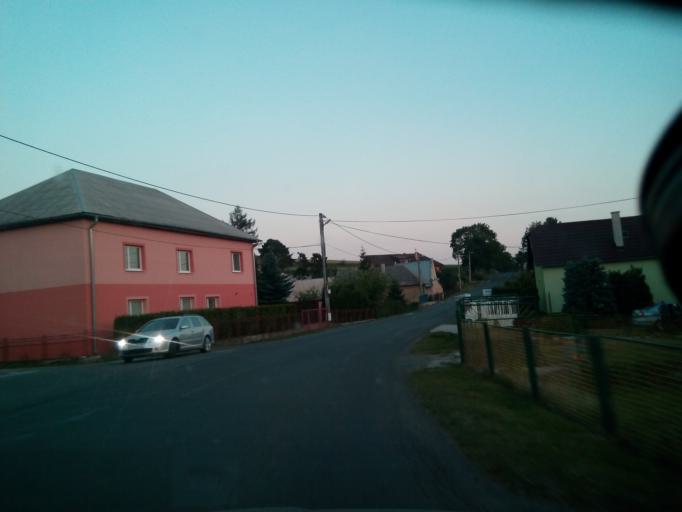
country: SK
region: Presovsky
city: Lubica
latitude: 49.0449
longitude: 20.4388
